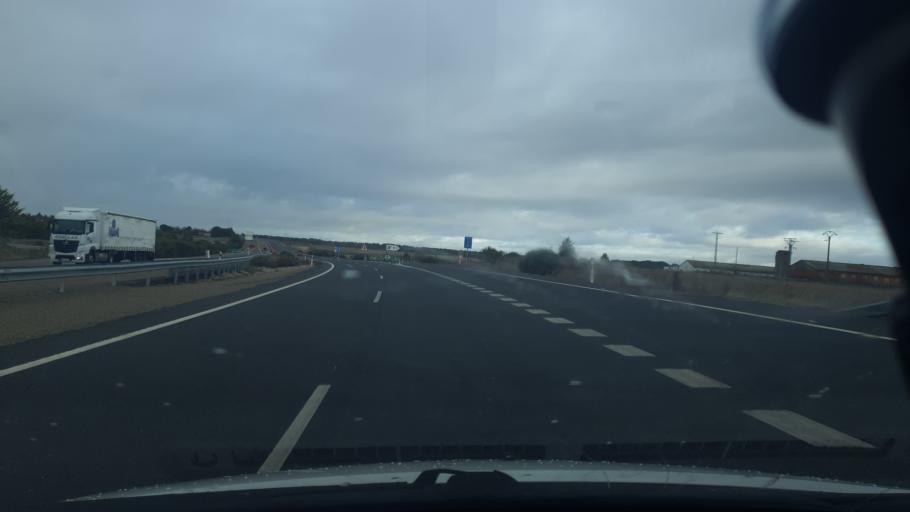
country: ES
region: Castille and Leon
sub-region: Provincia de Segovia
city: Cuellar
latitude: 41.4049
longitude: -4.2941
